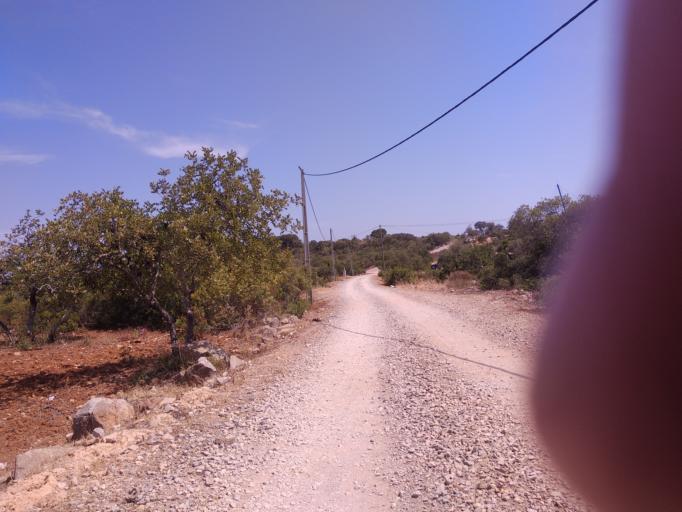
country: PT
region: Faro
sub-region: Faro
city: Santa Barbara de Nexe
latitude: 37.0934
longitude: -7.9747
